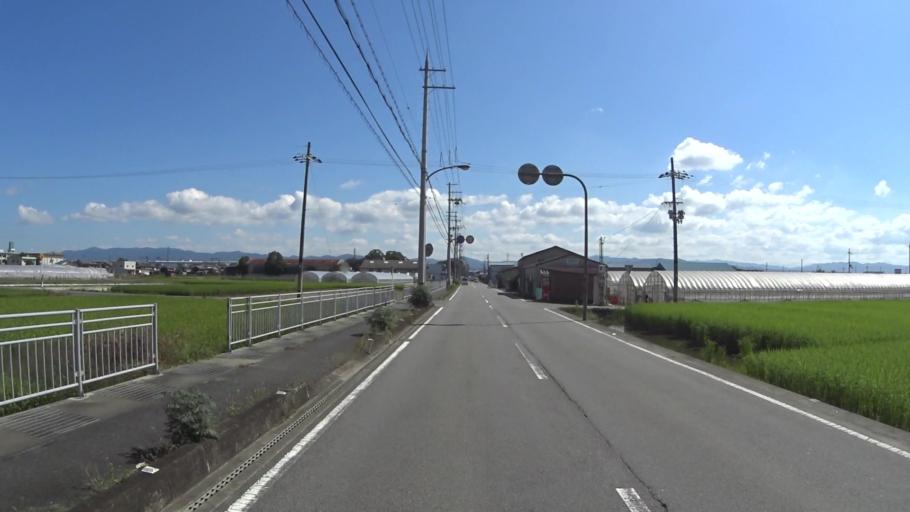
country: JP
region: Kyoto
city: Yawata
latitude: 34.8922
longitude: 135.7338
